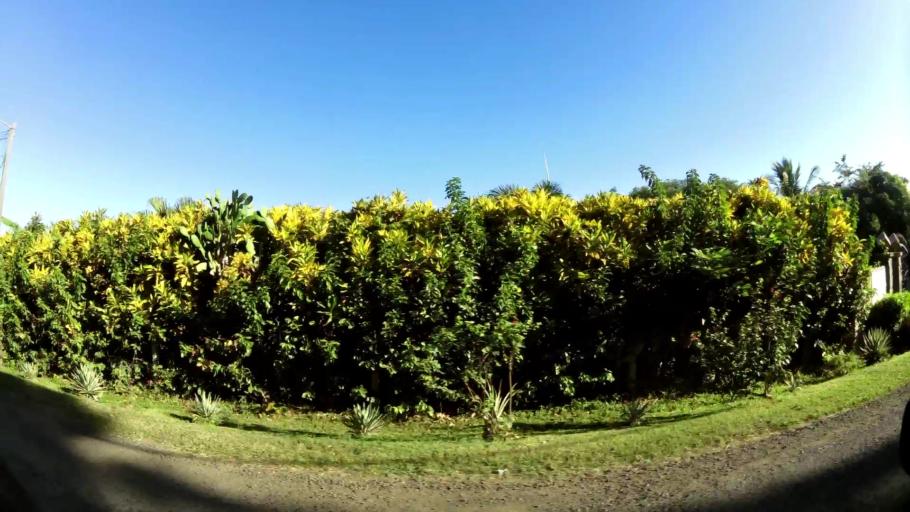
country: CR
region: Guanacaste
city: Sardinal
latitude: 10.5693
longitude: -85.6785
